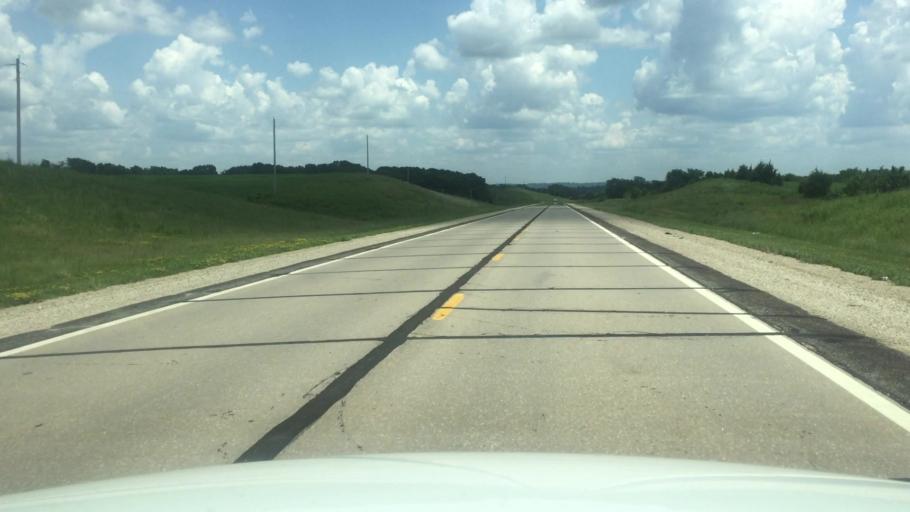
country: US
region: Kansas
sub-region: Atchison County
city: Atchison
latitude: 39.5572
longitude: -95.1702
